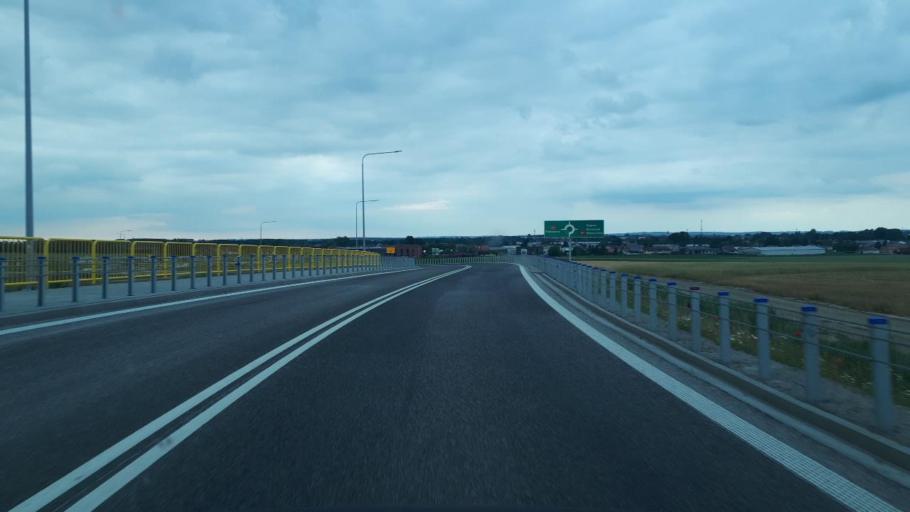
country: PL
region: Greater Poland Voivodeship
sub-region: Powiat kepinski
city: Baranow
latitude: 51.2564
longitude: 18.0136
